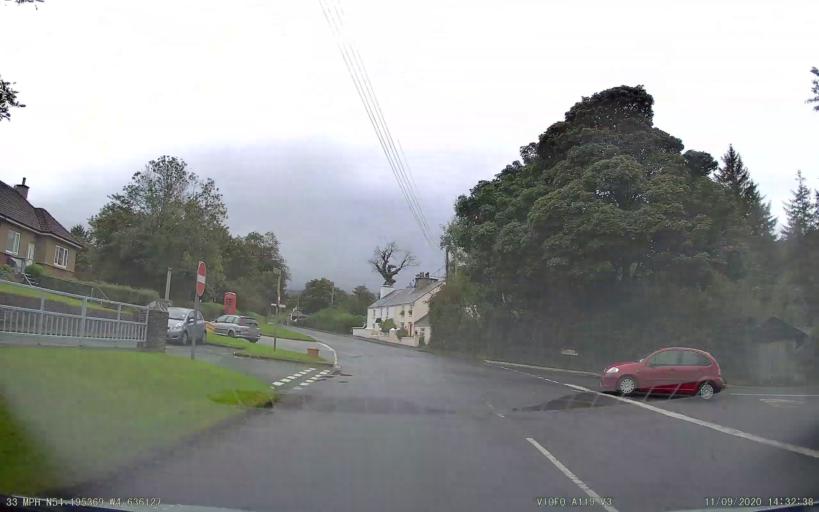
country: IM
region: Castletown
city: Castletown
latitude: 54.1954
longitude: -4.6362
